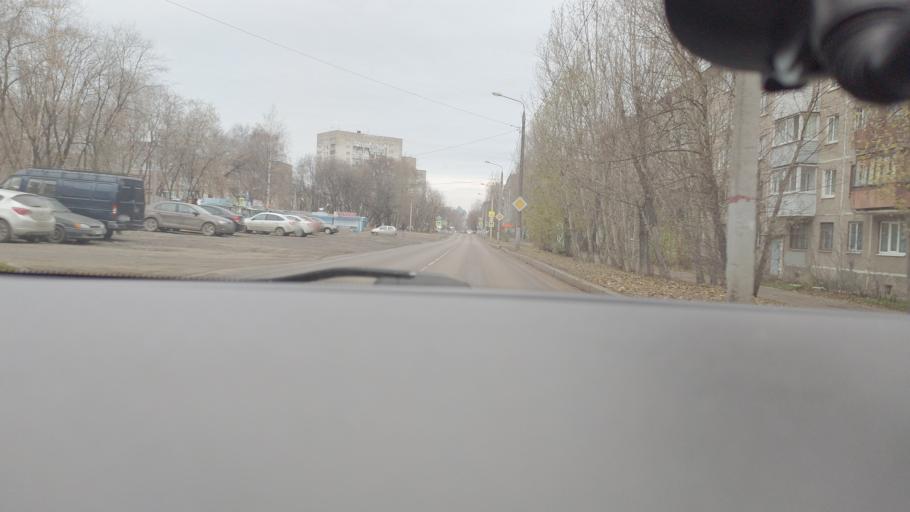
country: RU
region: Perm
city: Perm
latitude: 57.9906
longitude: 56.2329
